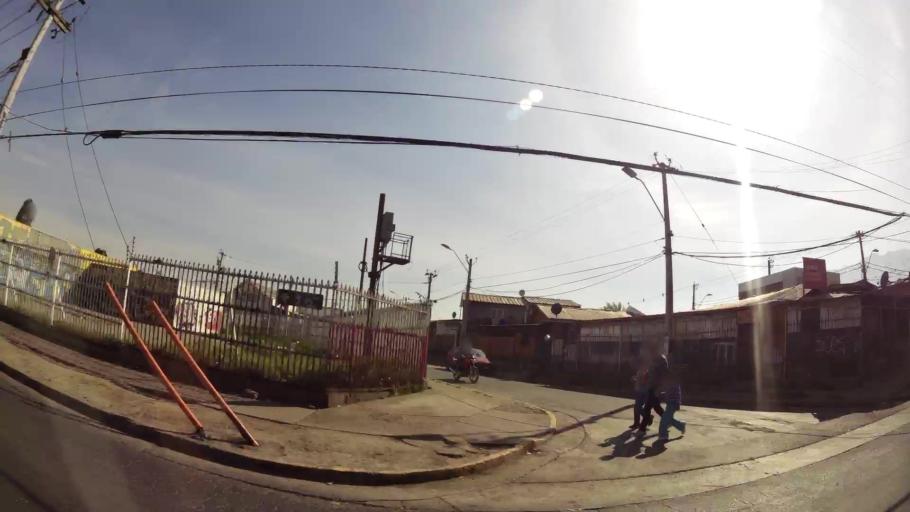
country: CL
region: Santiago Metropolitan
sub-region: Provincia de Santiago
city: Villa Presidente Frei, Nunoa, Santiago, Chile
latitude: -33.5038
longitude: -70.5686
